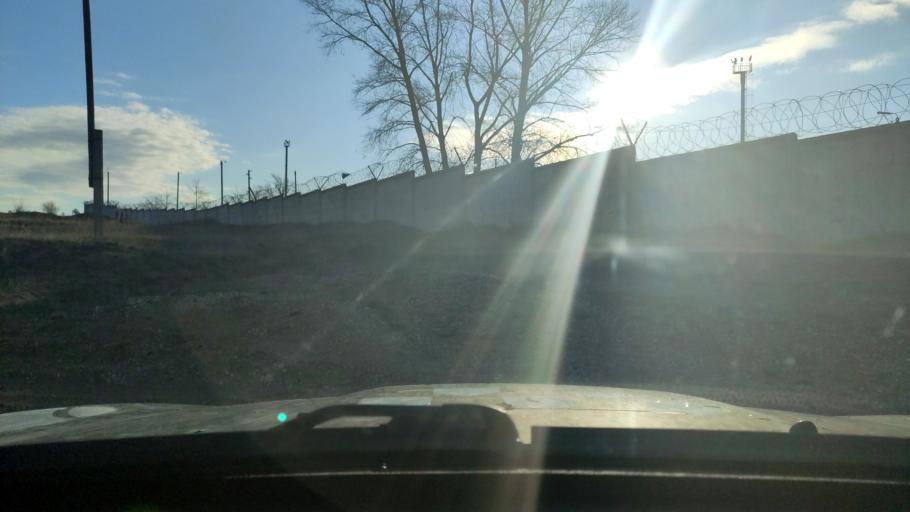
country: RU
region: Samara
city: Zhigulevsk
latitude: 53.4795
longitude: 49.5345
